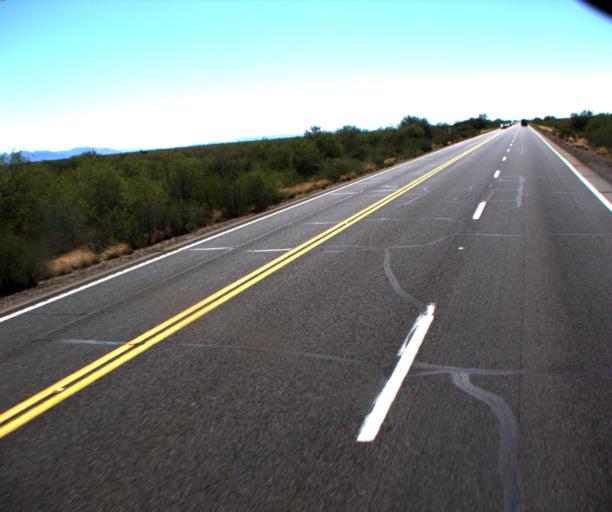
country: US
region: Arizona
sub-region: Yavapai County
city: Congress
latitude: 34.1523
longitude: -112.9921
